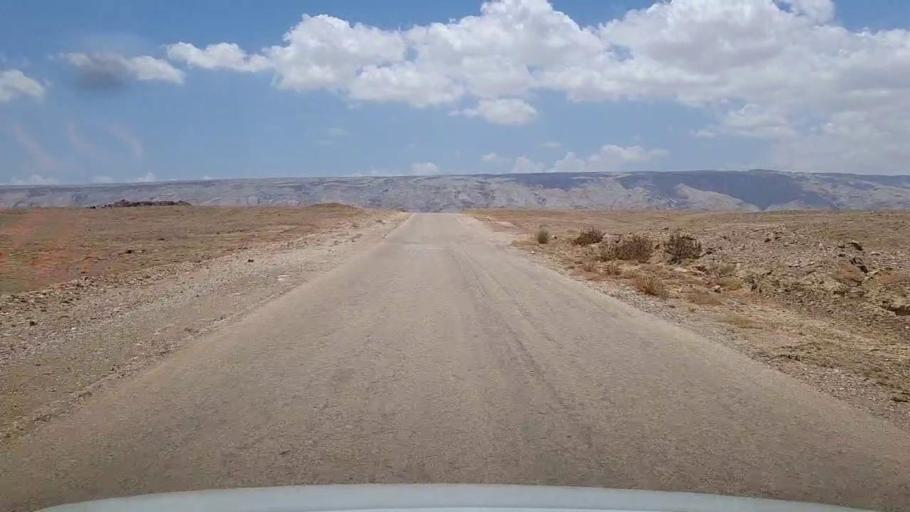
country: PK
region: Sindh
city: Bhan
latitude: 26.3198
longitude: 67.5469
